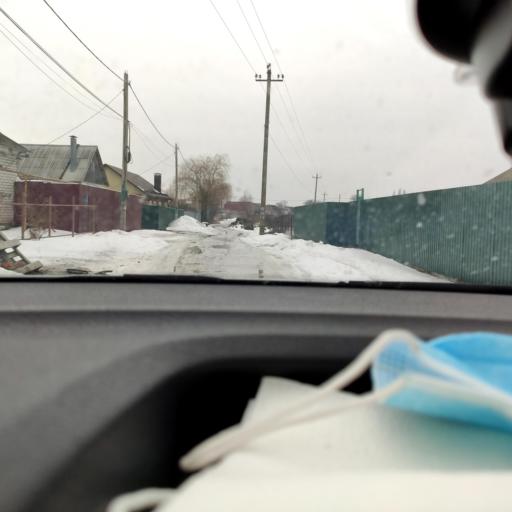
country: RU
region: Voronezj
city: Novaya Usman'
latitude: 51.6361
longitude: 39.3940
